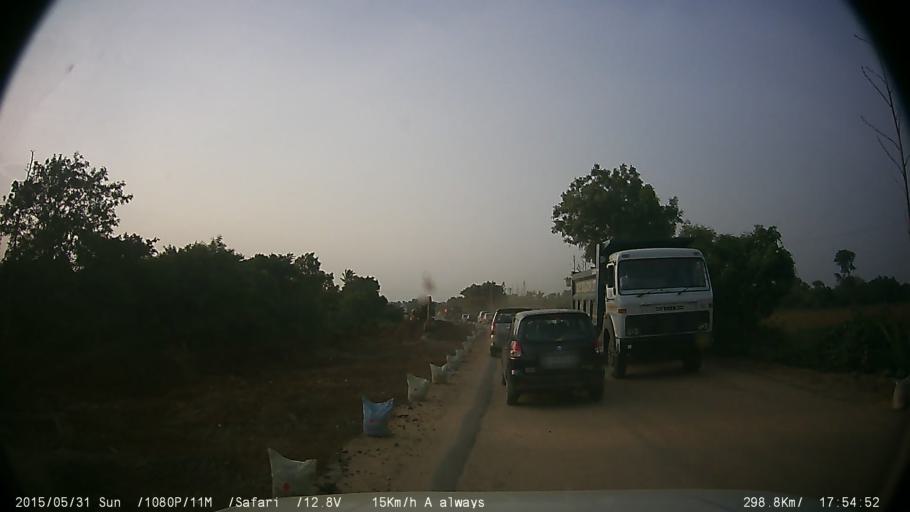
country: IN
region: Karnataka
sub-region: Mysore
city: Nanjangud
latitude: 11.9889
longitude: 76.6699
